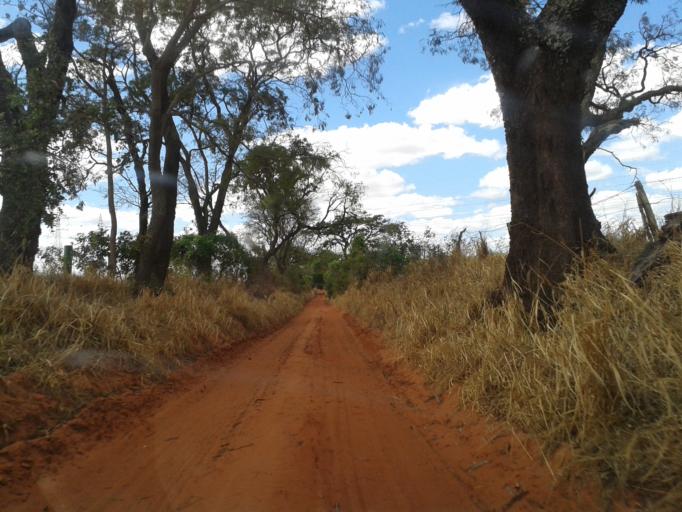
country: BR
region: Minas Gerais
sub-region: Monte Alegre De Minas
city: Monte Alegre de Minas
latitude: -18.7758
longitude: -49.0774
